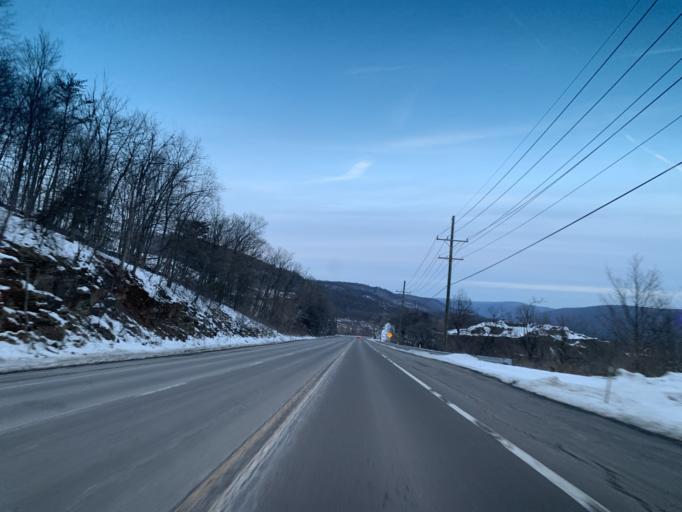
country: US
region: Maryland
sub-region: Allegany County
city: Cumberland
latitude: 39.7056
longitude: -78.6162
